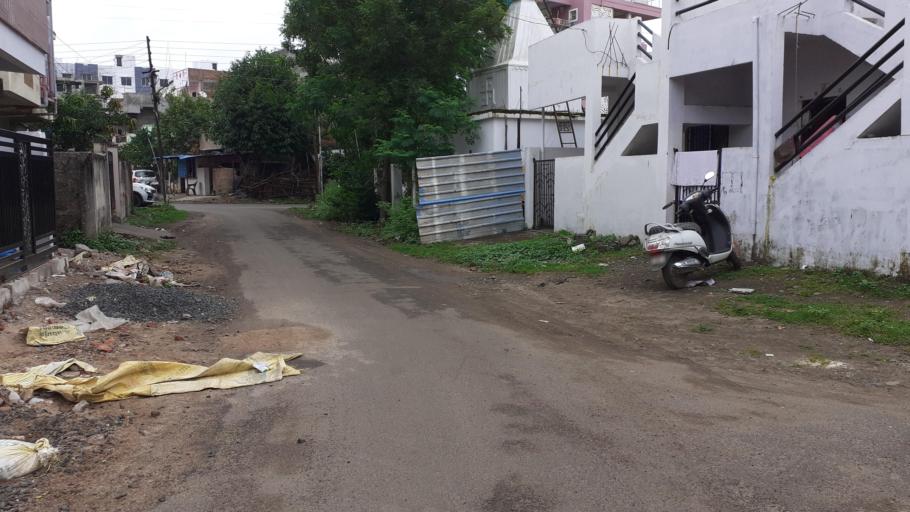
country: IN
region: Maharashtra
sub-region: Nagpur Division
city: Nagpur
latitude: 21.0978
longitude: 79.1141
